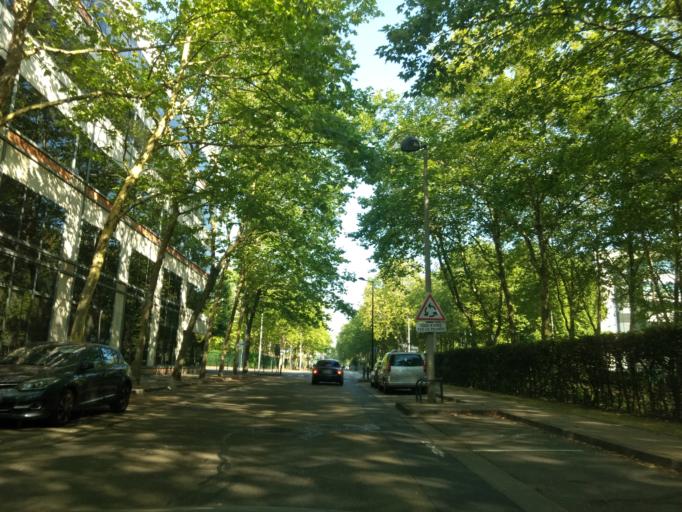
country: FR
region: Ile-de-France
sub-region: Departement des Yvelines
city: Saint-Cyr-l'Ecole
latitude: 48.7867
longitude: 2.0553
